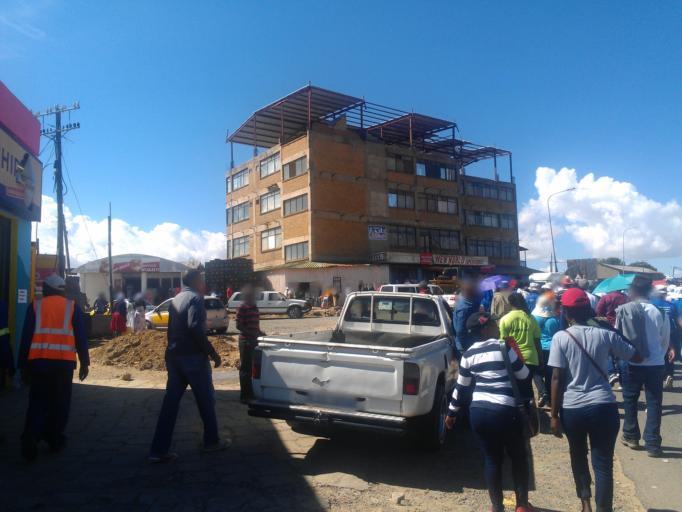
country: LS
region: Berea
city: Teyateyaneng
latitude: -29.1479
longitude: 27.7486
